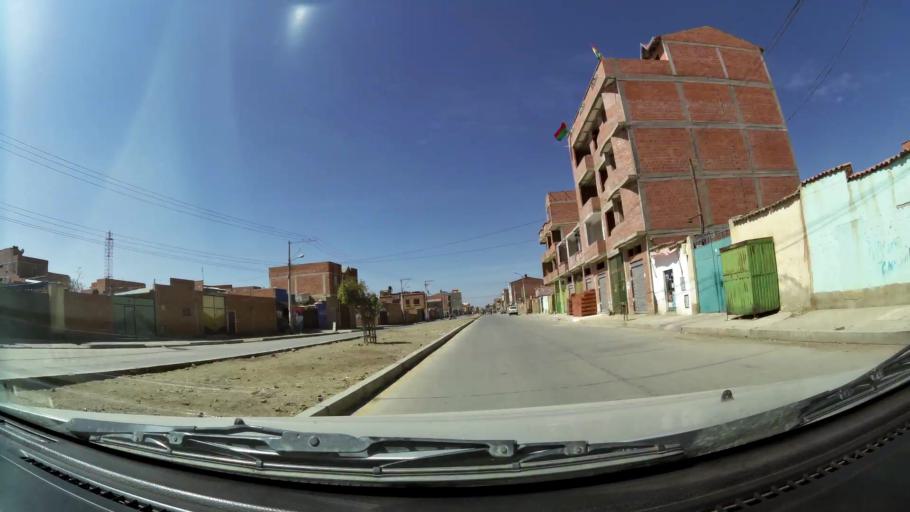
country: BO
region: La Paz
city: La Paz
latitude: -16.5365
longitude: -68.1585
